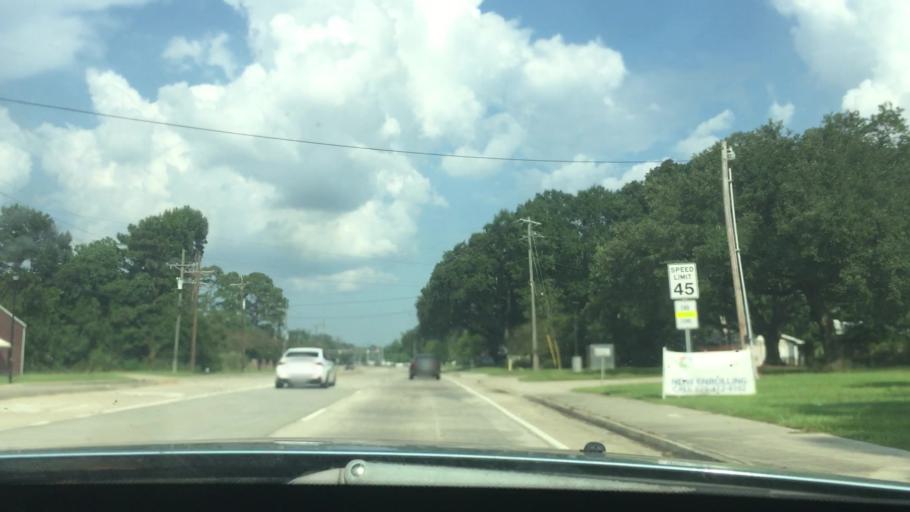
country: US
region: Louisiana
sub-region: East Baton Rouge Parish
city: Shenandoah
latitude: 30.4279
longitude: -91.0181
